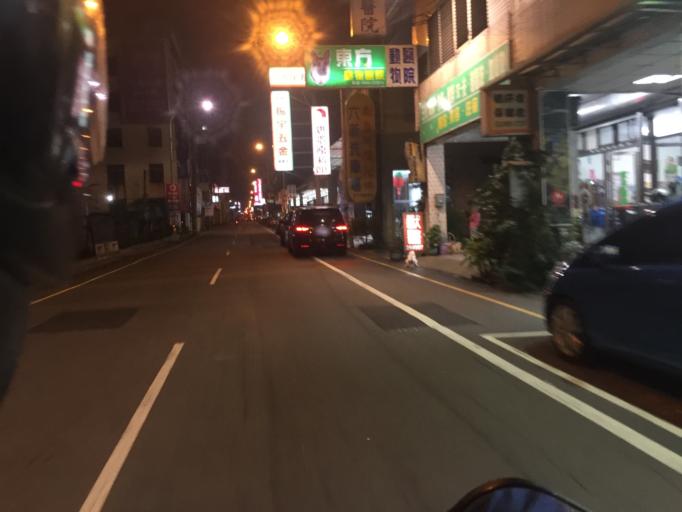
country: TW
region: Taiwan
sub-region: Miaoli
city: Miaoli
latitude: 24.5682
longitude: 120.8236
